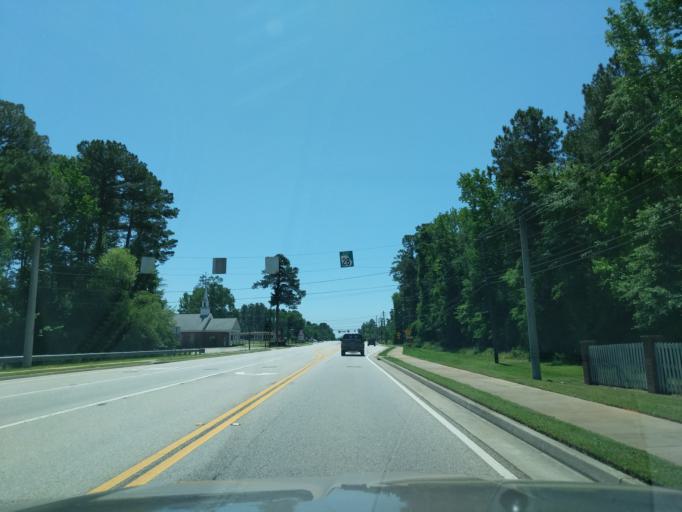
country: US
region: Georgia
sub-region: Columbia County
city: Martinez
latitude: 33.5529
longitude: -82.0919
